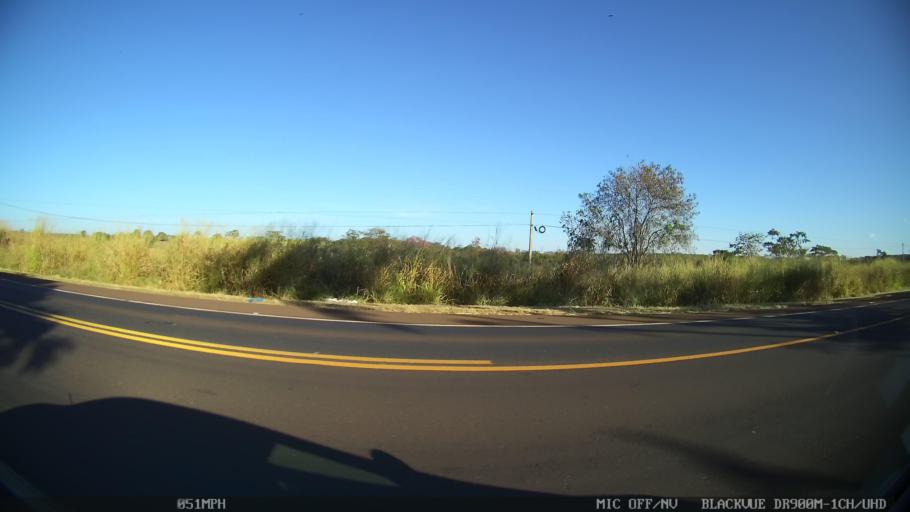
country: BR
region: Sao Paulo
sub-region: Olimpia
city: Olimpia
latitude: -20.7099
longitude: -48.9728
